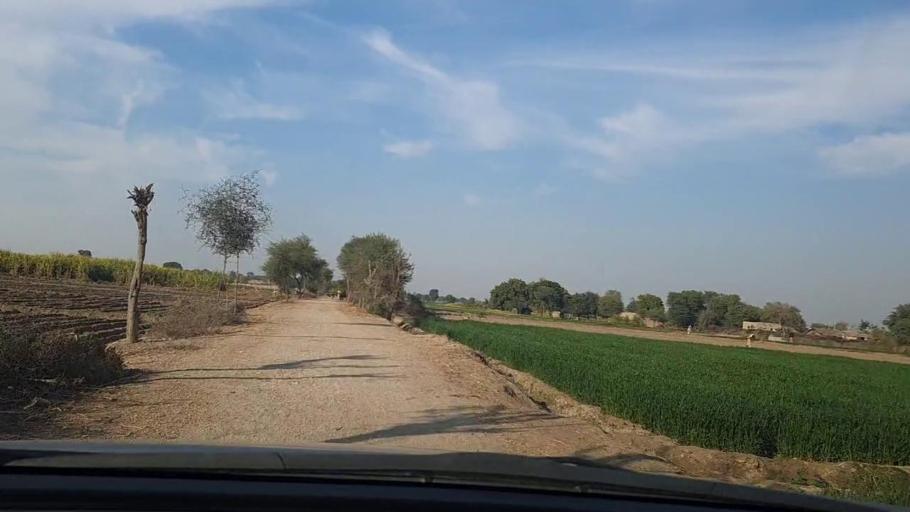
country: PK
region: Sindh
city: Sehwan
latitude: 26.3127
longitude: 68.0204
